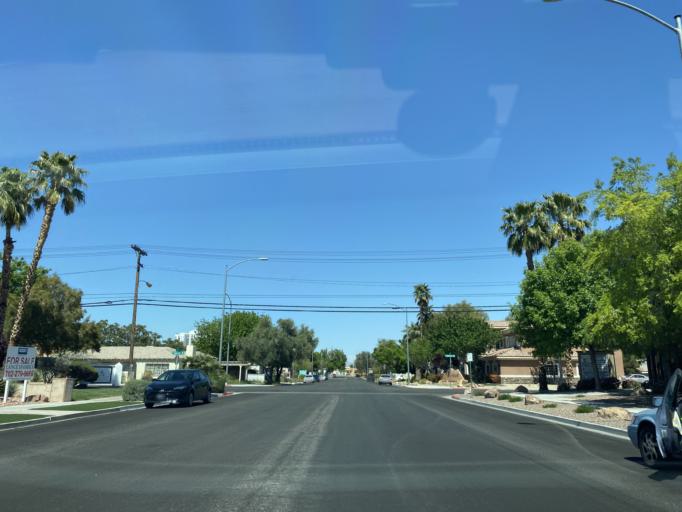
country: US
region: Nevada
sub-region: Clark County
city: Las Vegas
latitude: 36.1603
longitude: -115.1421
